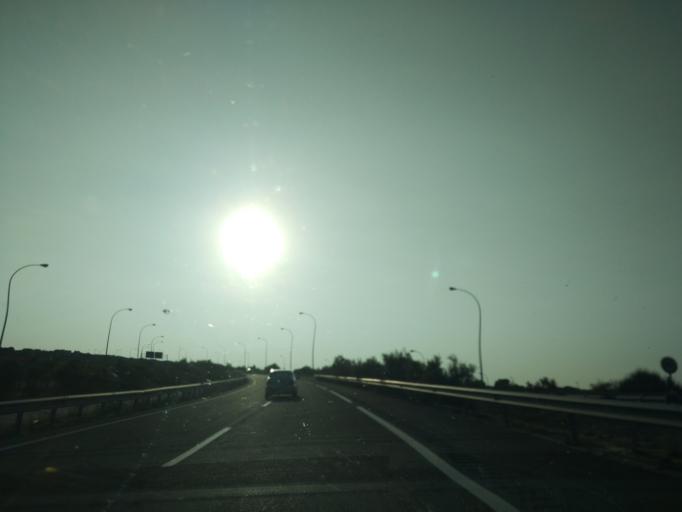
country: ES
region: Castille and Leon
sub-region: Provincia de Avila
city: Berrocalejo de Aragona
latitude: 40.6785
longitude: -4.6317
